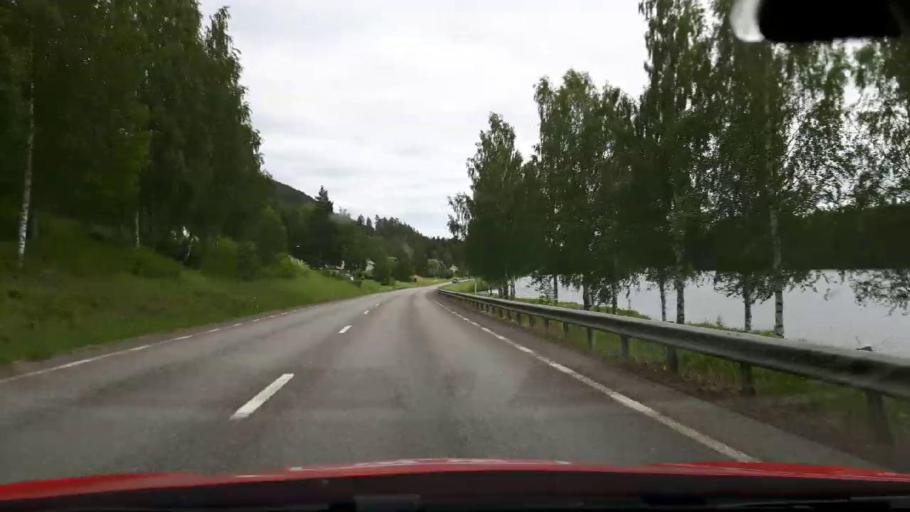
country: SE
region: Jaemtland
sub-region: Ragunda Kommun
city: Hammarstrand
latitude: 63.1424
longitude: 16.3359
